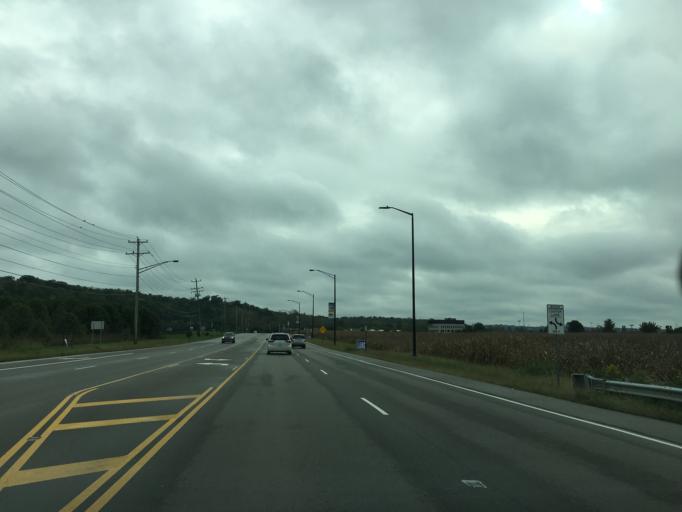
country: US
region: Ohio
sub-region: Butler County
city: Beckett Ridge
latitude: 39.3383
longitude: -84.4431
